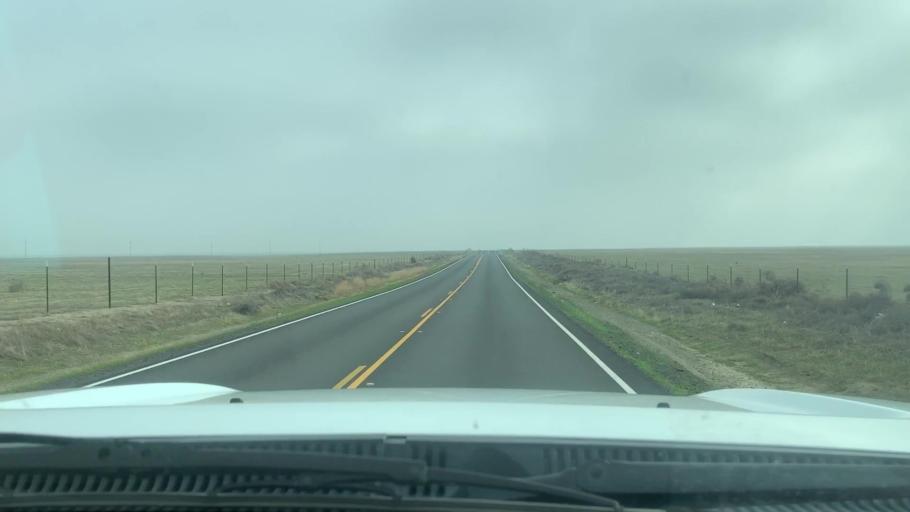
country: US
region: California
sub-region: Kern County
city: Lost Hills
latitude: 35.6007
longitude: -119.8502
